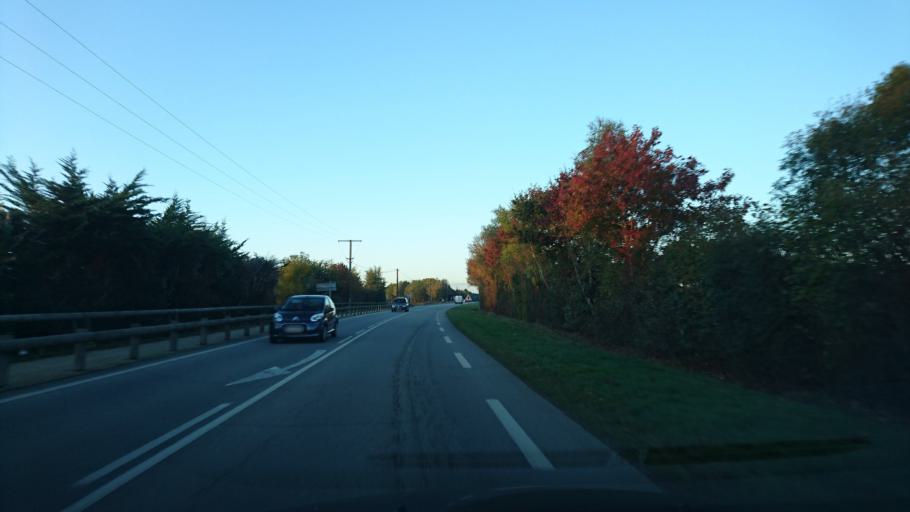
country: FR
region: Brittany
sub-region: Departement du Morbihan
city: Le Bono
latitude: 47.6502
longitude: -2.9614
